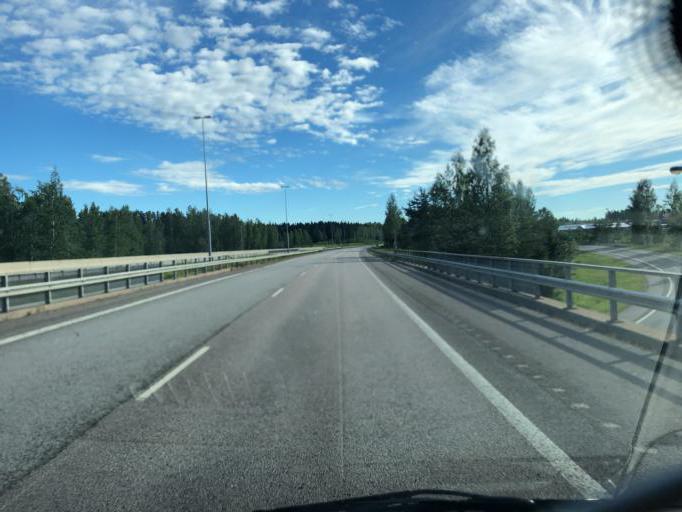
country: FI
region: Uusimaa
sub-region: Porvoo
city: Porvoo
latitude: 60.3926
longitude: 25.6183
